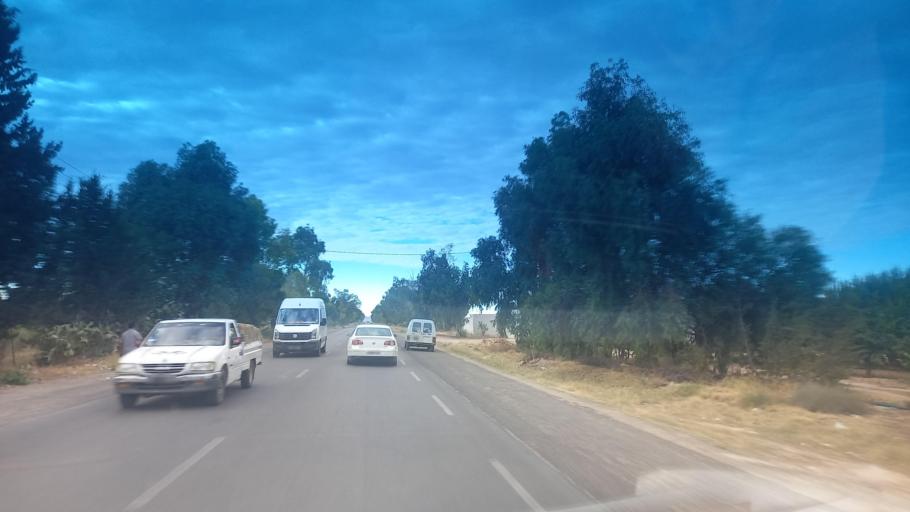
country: TN
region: Al Qasrayn
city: Sbiba
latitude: 35.2963
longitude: 9.0897
